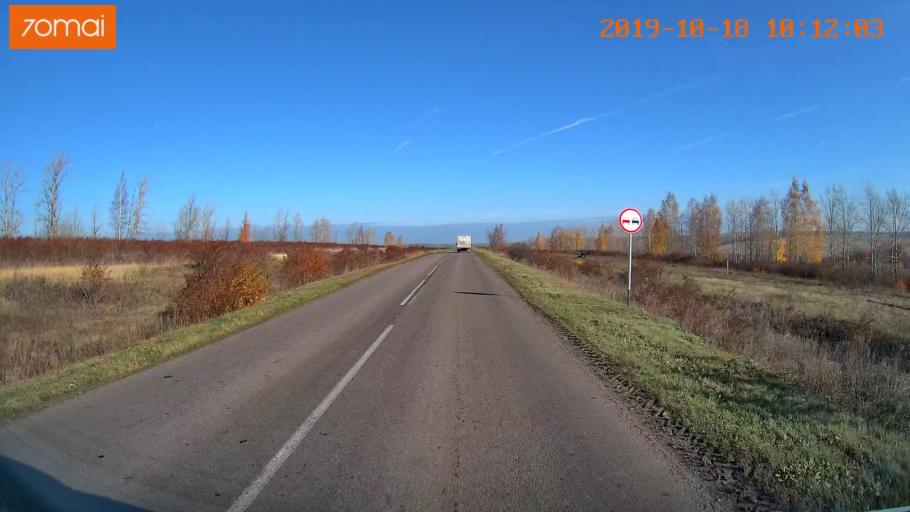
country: RU
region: Tula
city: Kurkino
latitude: 53.3895
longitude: 38.5048
